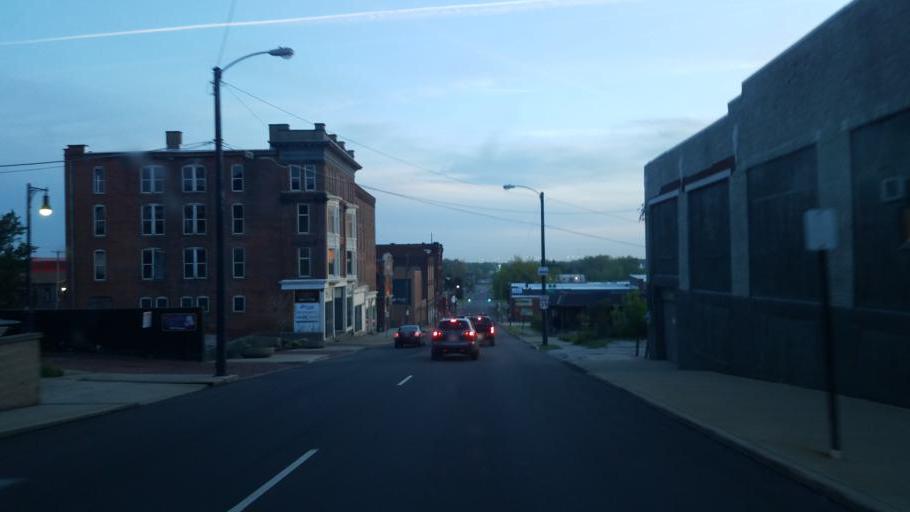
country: US
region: Ohio
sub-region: Richland County
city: Mansfield
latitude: 40.7611
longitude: -82.5139
